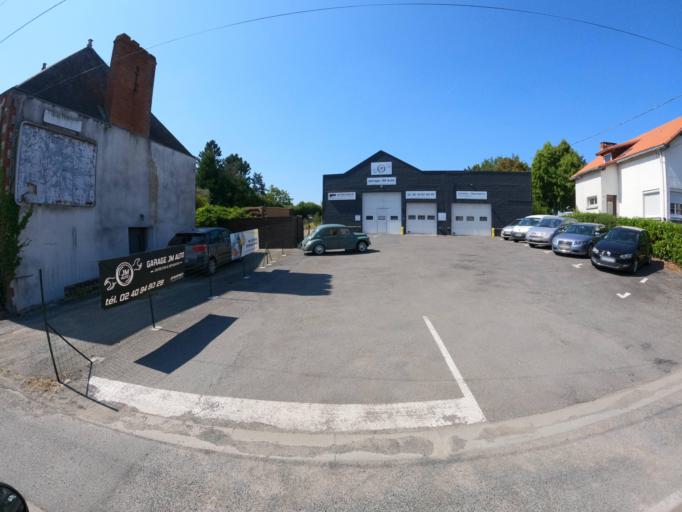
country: FR
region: Pays de la Loire
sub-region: Departement de la Loire-Atlantique
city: Montbert
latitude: 47.0601
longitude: -1.4910
